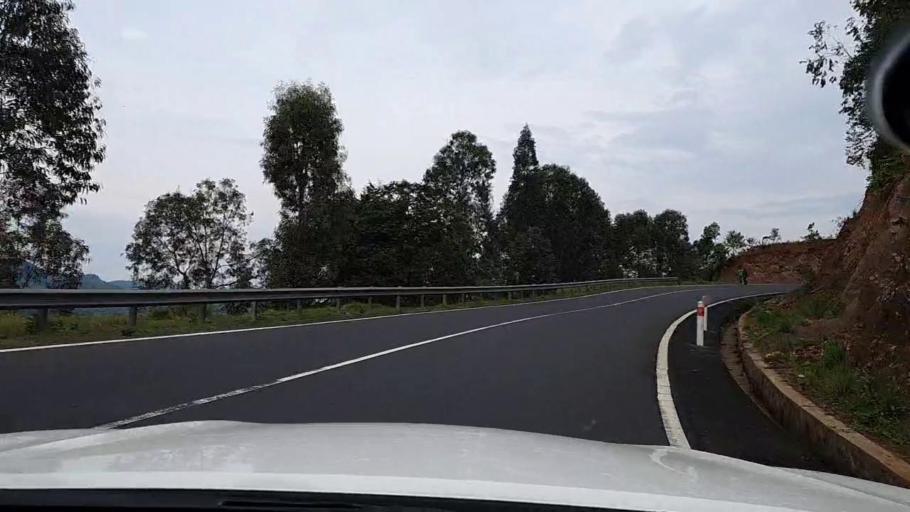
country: RW
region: Western Province
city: Kibuye
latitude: -2.1815
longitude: 29.2891
